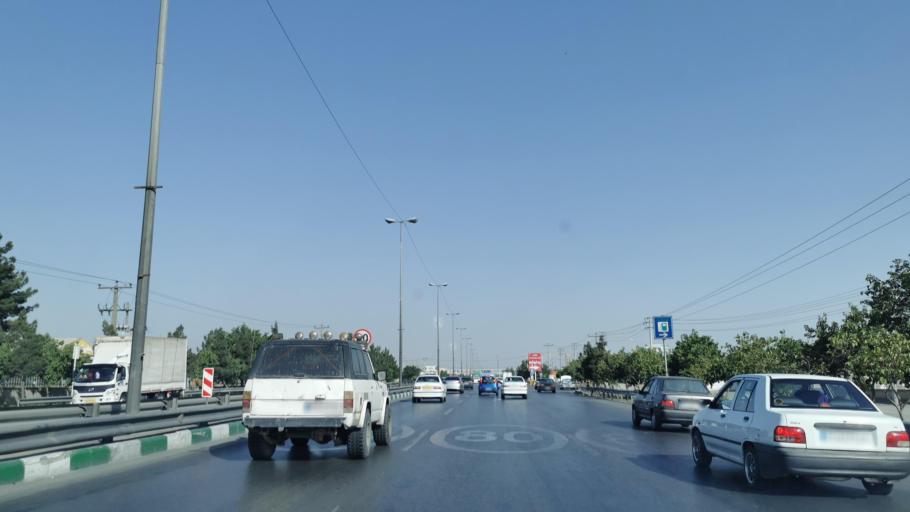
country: IR
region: Razavi Khorasan
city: Mashhad
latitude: 36.3932
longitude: 59.5025
